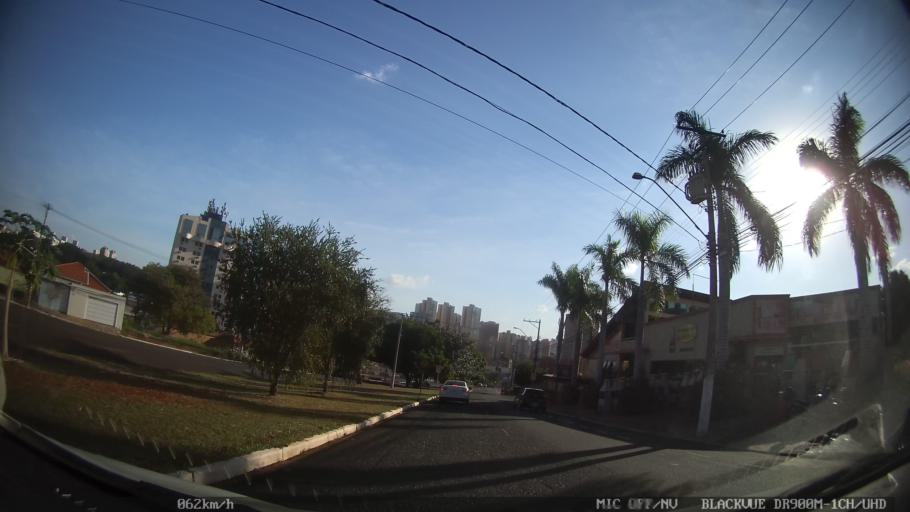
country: BR
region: Sao Paulo
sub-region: Ribeirao Preto
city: Ribeirao Preto
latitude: -21.2066
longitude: -47.7875
